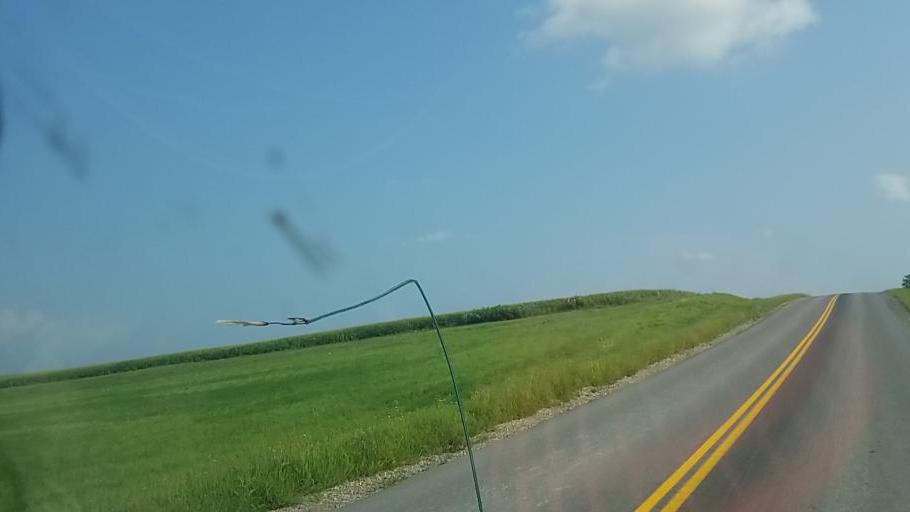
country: US
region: New York
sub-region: Montgomery County
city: Fonda
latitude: 42.9041
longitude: -74.3683
